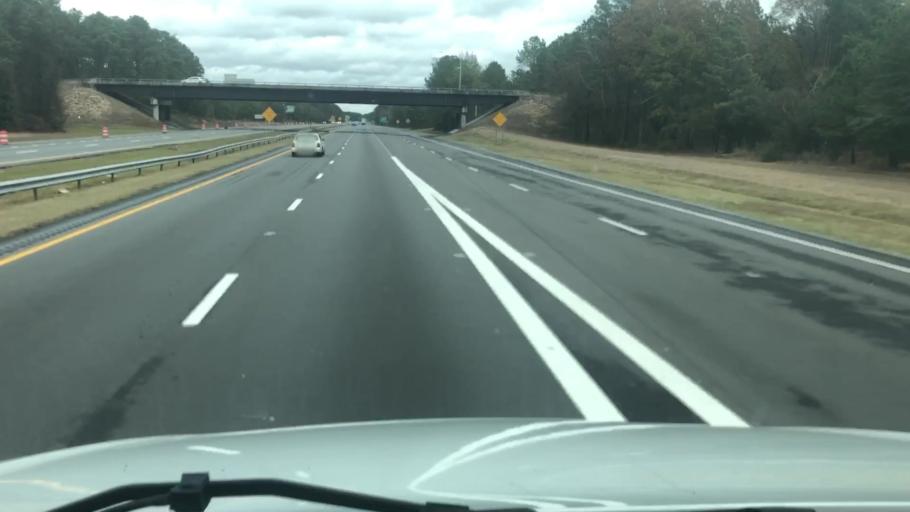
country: US
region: North Carolina
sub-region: Cumberland County
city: Eastover
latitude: 35.0945
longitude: -78.7780
